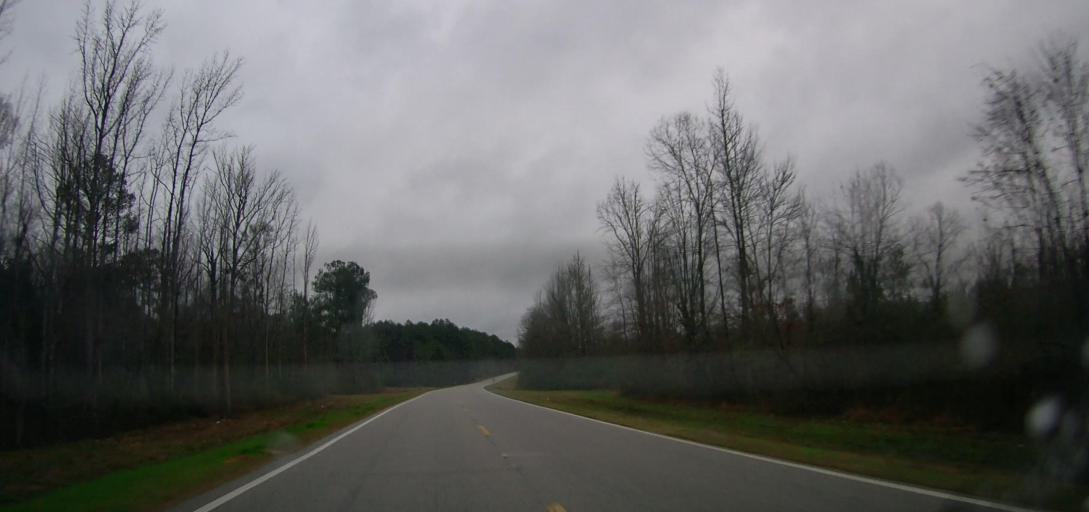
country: US
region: Alabama
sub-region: Bibb County
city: Centreville
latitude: 32.9193
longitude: -87.0314
